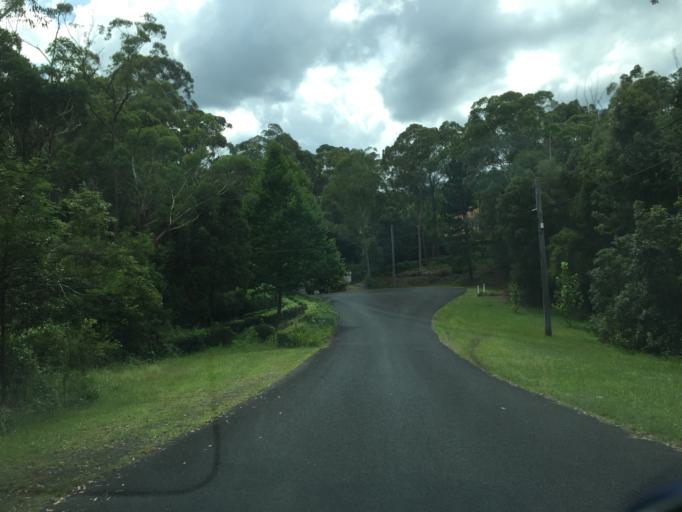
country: AU
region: New South Wales
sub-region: Hornsby Shire
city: Galston
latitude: -33.6590
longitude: 151.0498
